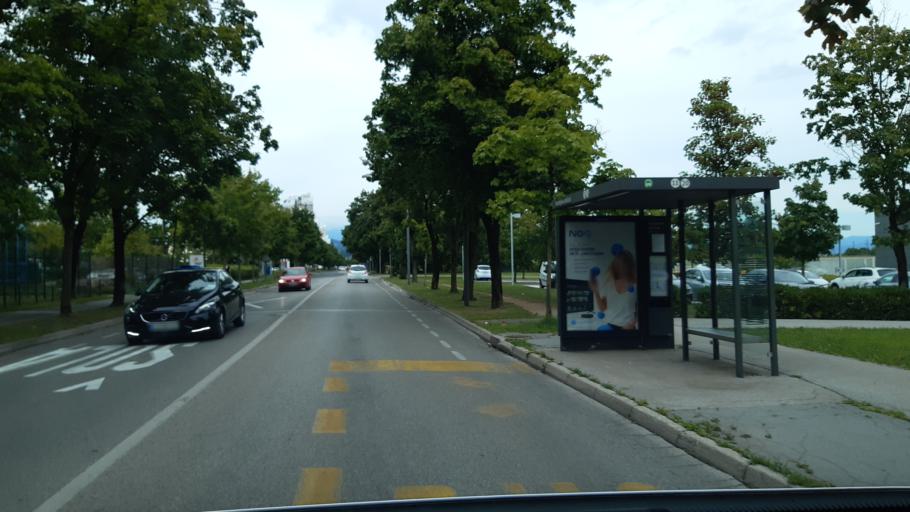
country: SI
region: Ljubljana
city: Ljubljana
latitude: 46.0725
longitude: 14.5193
